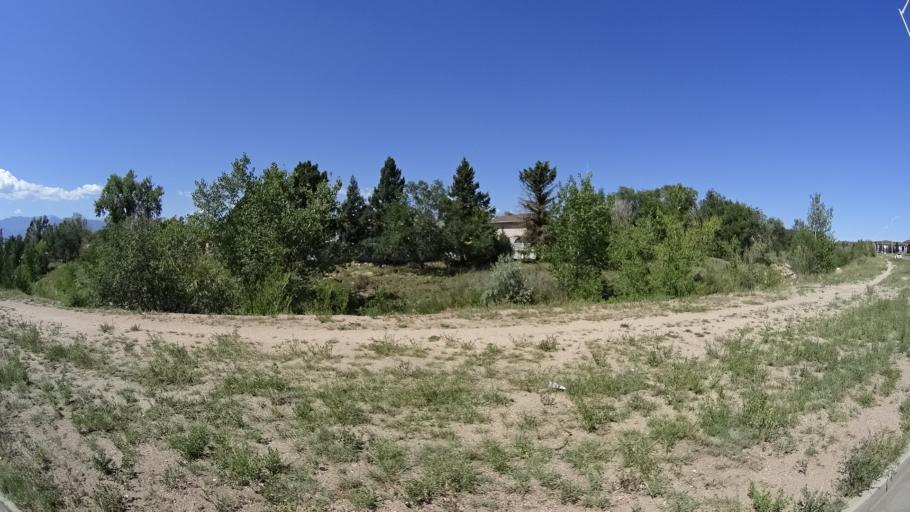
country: US
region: Colorado
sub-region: El Paso County
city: Cimarron Hills
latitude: 38.8474
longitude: -104.7225
